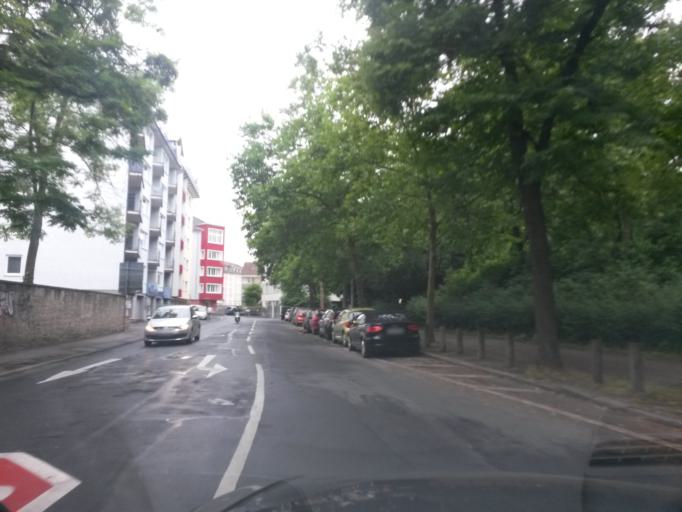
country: DE
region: Bavaria
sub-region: Regierungsbezirk Unterfranken
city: Wuerzburg
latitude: 49.7876
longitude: 9.9376
